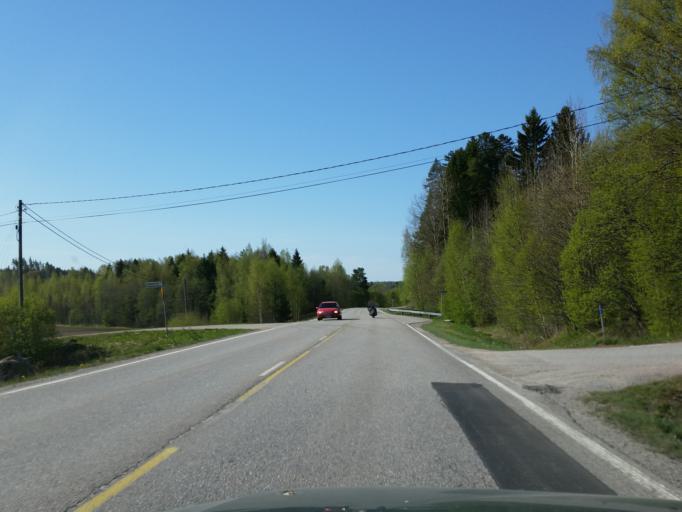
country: FI
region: Uusimaa
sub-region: Helsinki
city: Siuntio
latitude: 60.1811
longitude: 24.2351
